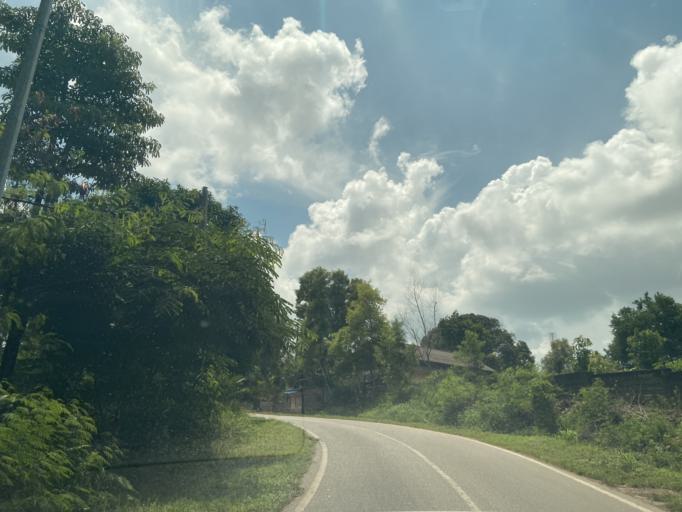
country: SG
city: Singapore
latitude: 1.1549
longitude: 104.0102
